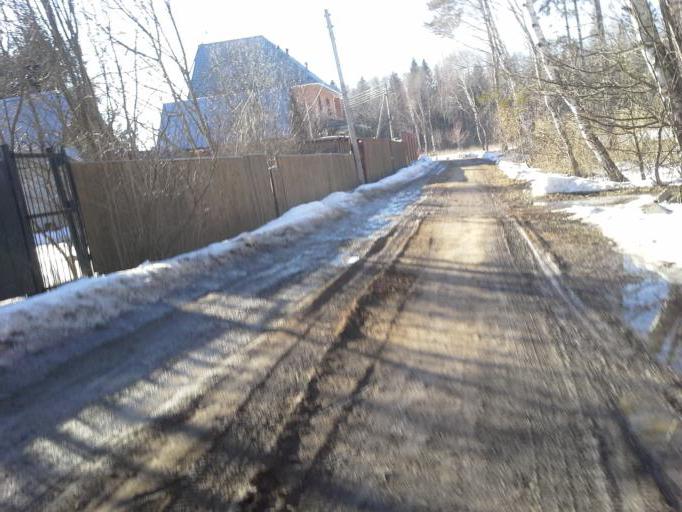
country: RU
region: Moskovskaya
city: Filimonki
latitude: 55.5479
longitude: 37.3814
